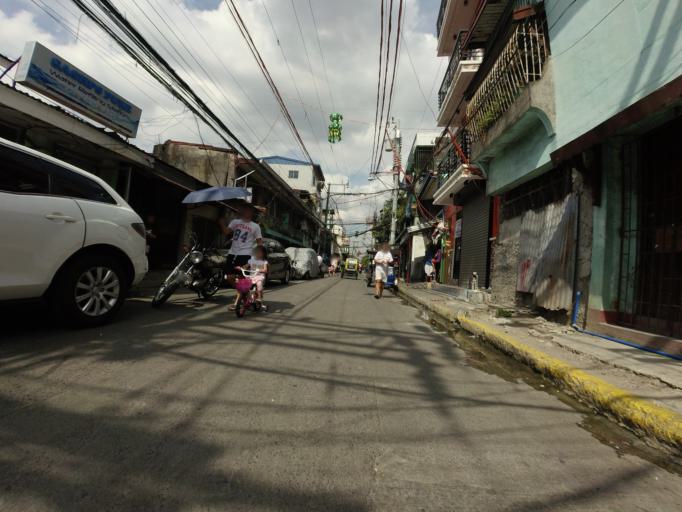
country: PH
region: Metro Manila
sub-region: City of Manila
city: Quiapo
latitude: 14.5725
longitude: 120.9963
